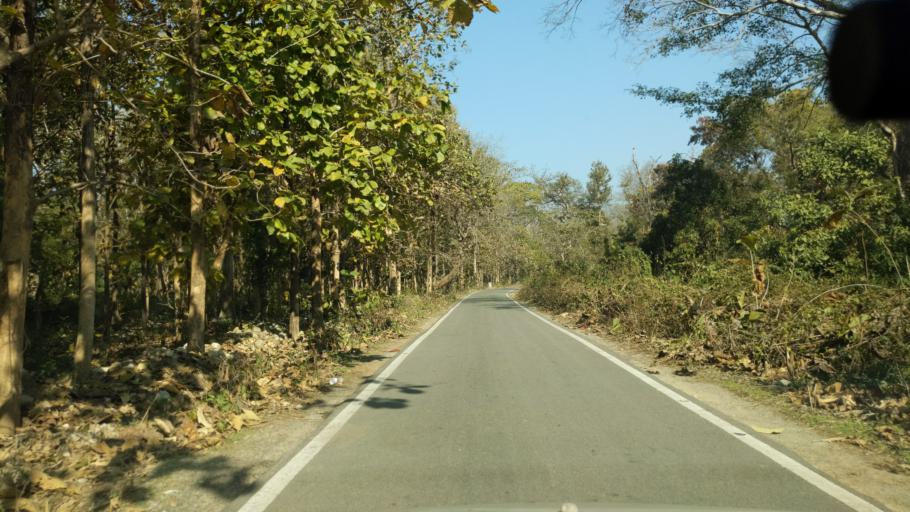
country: IN
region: Uttarakhand
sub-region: Naini Tal
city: Ramnagar
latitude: 29.4145
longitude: 79.1372
